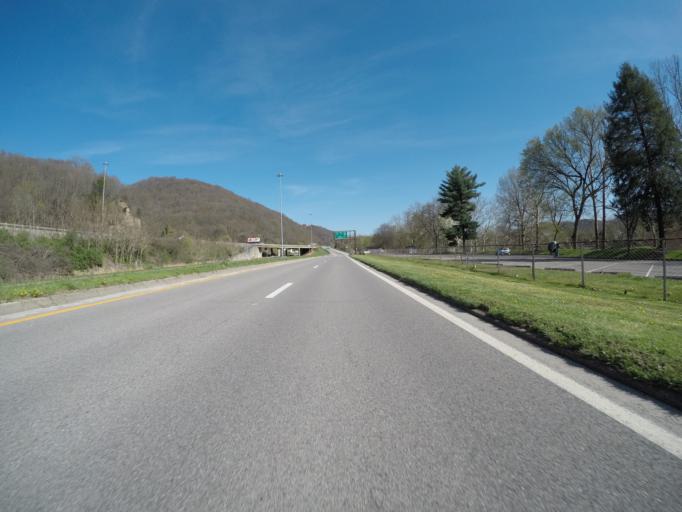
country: US
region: West Virginia
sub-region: Kanawha County
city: Rand
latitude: 38.3310
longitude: -81.5833
